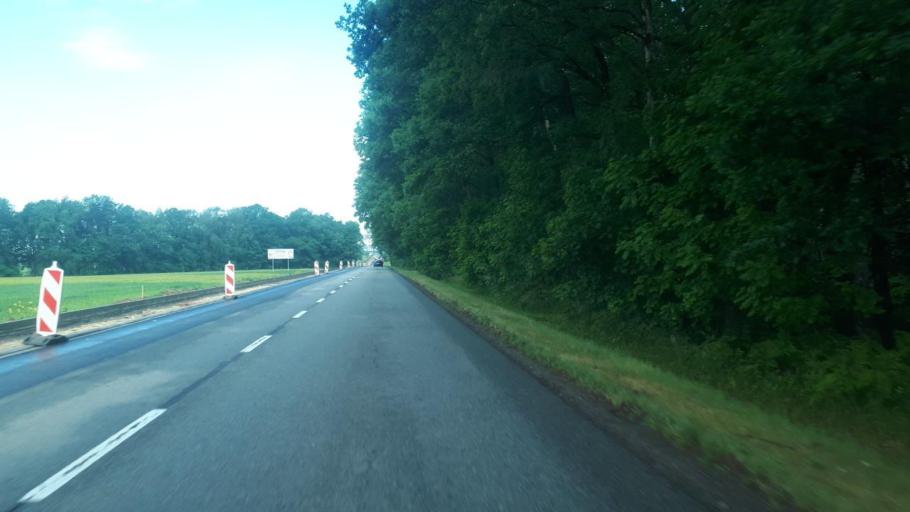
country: PL
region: Silesian Voivodeship
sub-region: Powiat pszczynski
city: Miedzna
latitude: 49.9706
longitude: 19.0173
